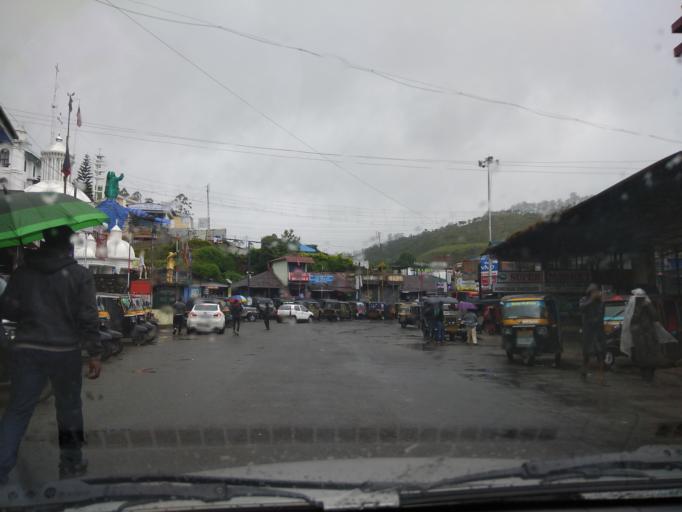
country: IN
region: Kerala
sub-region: Idukki
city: Munnar
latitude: 10.0870
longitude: 77.0600
